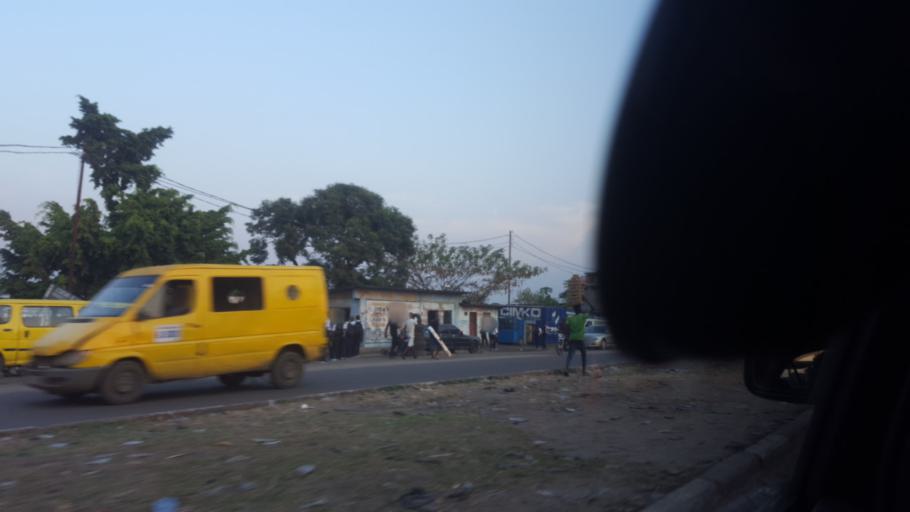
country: CD
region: Kinshasa
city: Kinshasa
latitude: -4.3449
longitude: 15.3250
